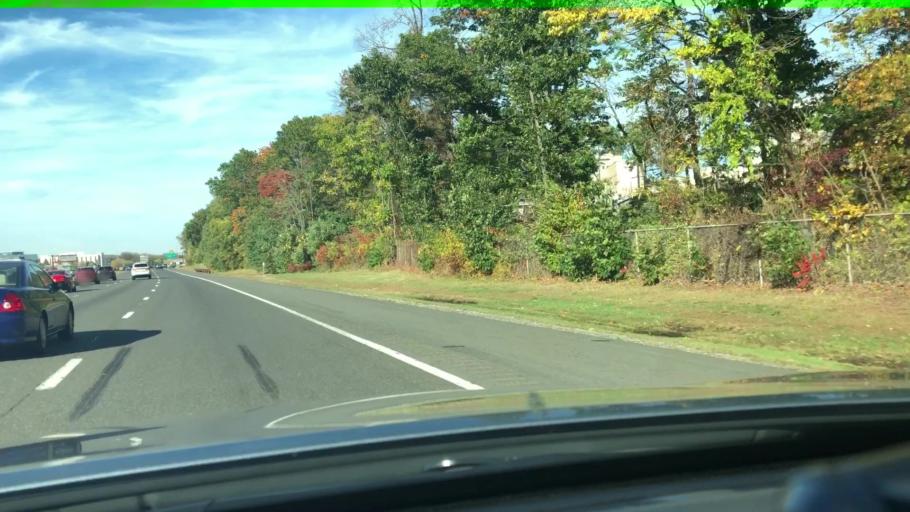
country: US
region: New Jersey
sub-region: Bergen County
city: Paramus
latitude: 40.9531
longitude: -74.0657
